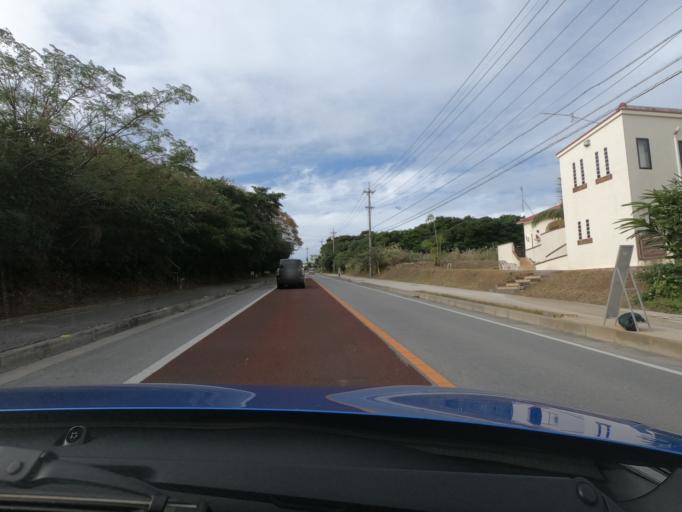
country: JP
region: Okinawa
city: Nago
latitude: 26.6796
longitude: 127.8873
